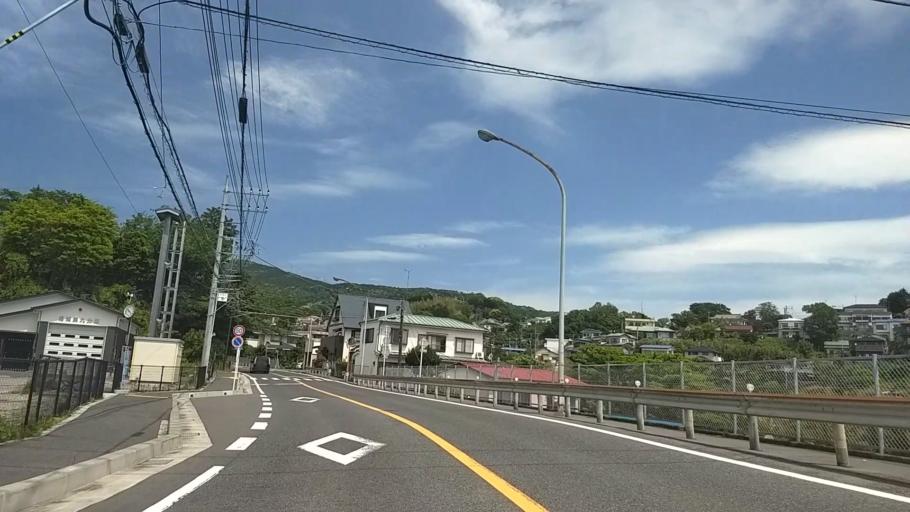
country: JP
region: Kanagawa
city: Yugawara
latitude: 35.1523
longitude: 139.1295
